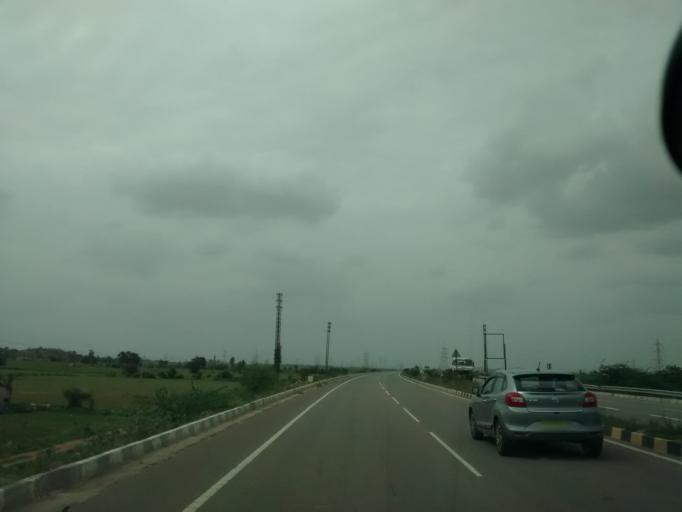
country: IN
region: Andhra Pradesh
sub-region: Kurnool
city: Ramapuram
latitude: 15.1196
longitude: 77.6605
